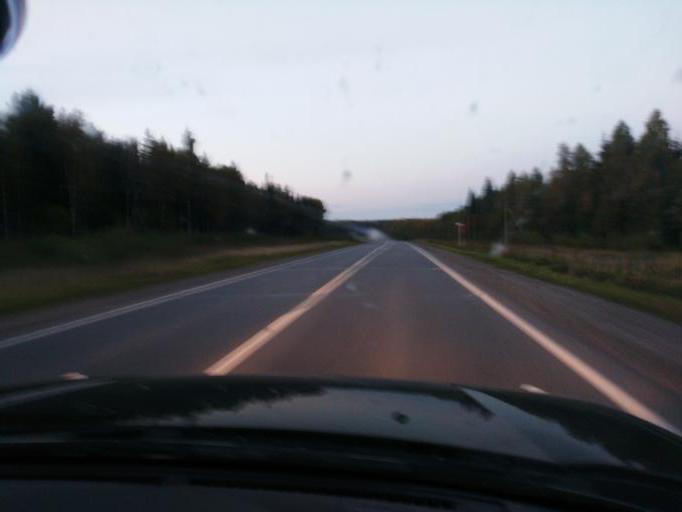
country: RU
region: Perm
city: Verkhnechusovskiye Gorodki
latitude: 58.2321
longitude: 57.2123
